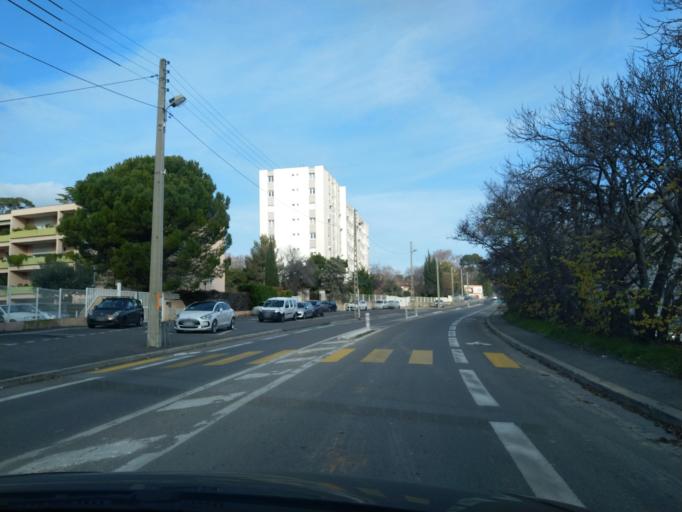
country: FR
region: Provence-Alpes-Cote d'Azur
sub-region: Departement des Bouches-du-Rhone
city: Marseille 12
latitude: 43.3001
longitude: 5.4368
